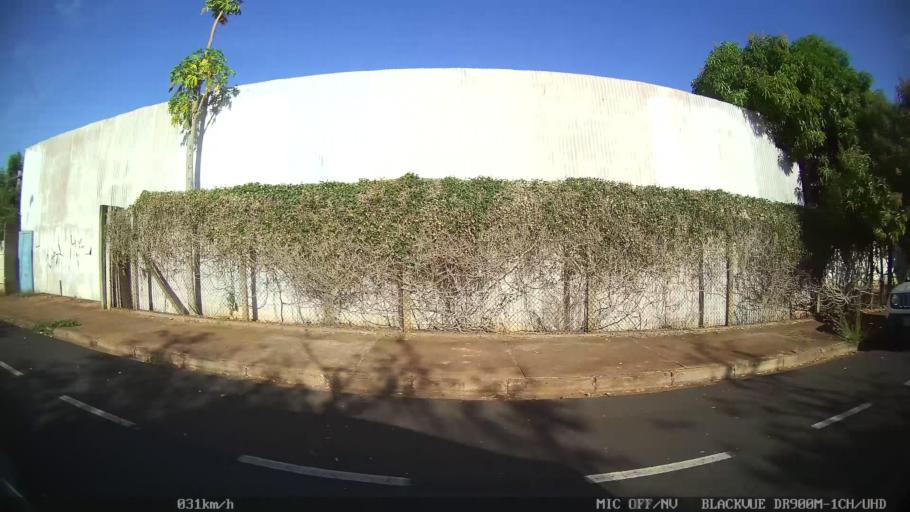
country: BR
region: Sao Paulo
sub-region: Sao Jose Do Rio Preto
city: Sao Jose do Rio Preto
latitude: -20.8166
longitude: -49.4038
